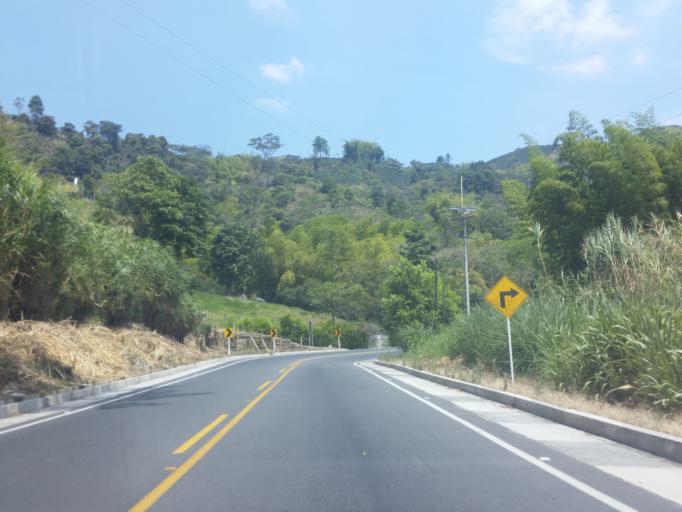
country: CO
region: Caldas
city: Chinchina
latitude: 4.9910
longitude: -75.5812
